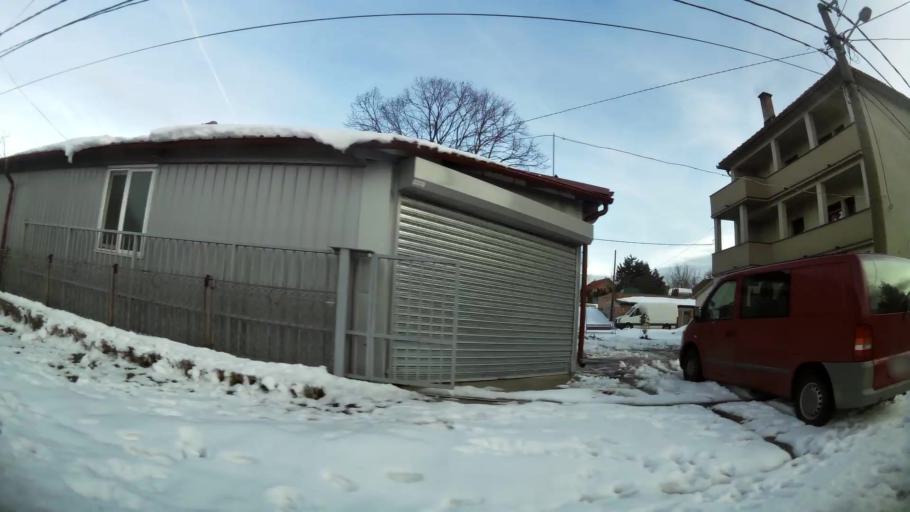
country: RS
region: Central Serbia
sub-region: Belgrade
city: Zvezdara
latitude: 44.7353
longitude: 20.5114
